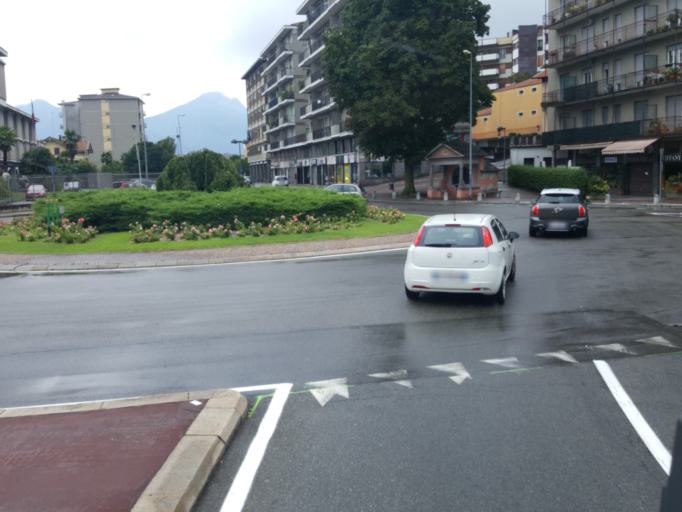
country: IT
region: Piedmont
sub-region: Provincia Verbano-Cusio-Ossola
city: Verbania
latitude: 45.9287
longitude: 8.5523
